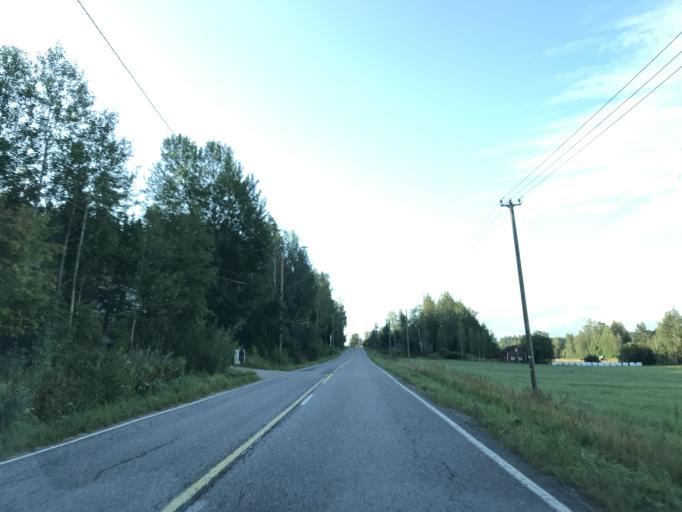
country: FI
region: Uusimaa
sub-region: Helsinki
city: Kauniainen
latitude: 60.3638
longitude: 24.6837
